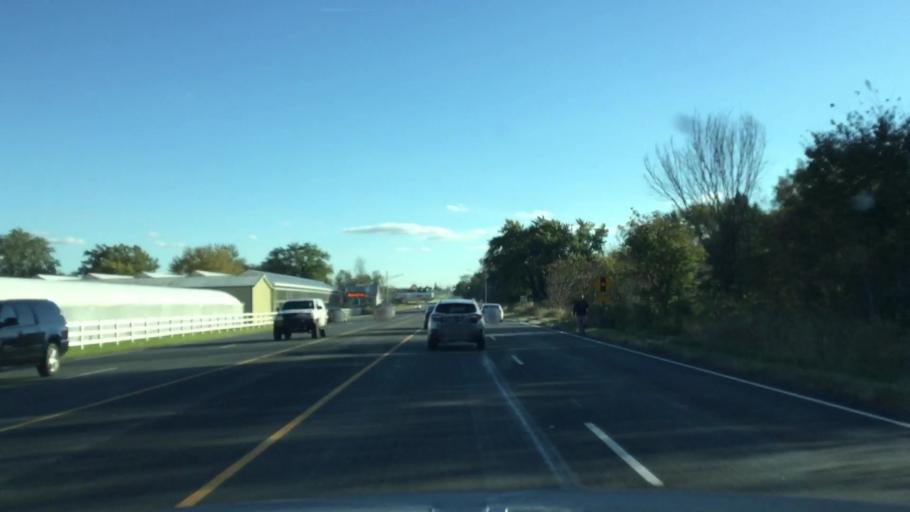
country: US
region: Michigan
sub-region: Kalamazoo County
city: Eastwood
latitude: 42.2797
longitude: -85.5307
